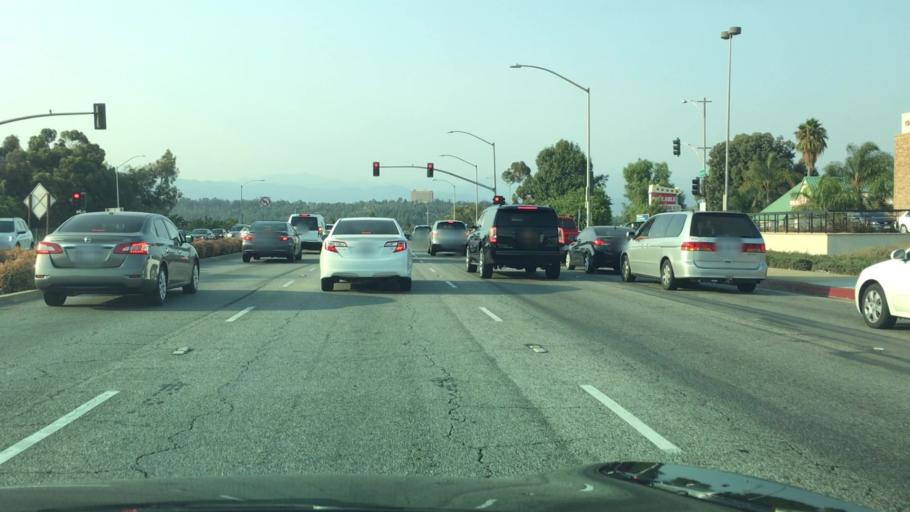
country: US
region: California
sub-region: Los Angeles County
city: La Puente
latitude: 33.9953
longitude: -117.9313
